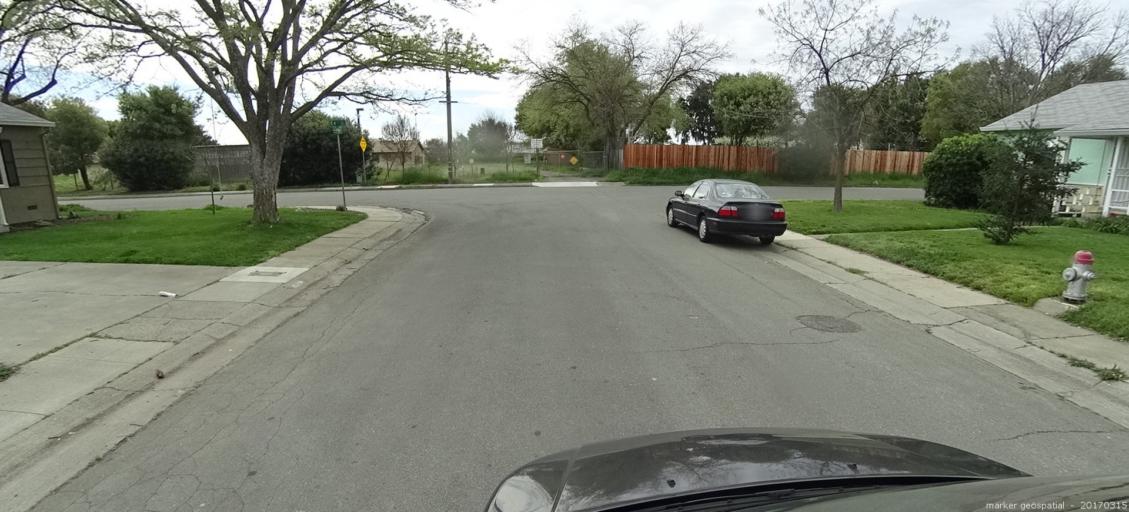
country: US
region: California
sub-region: Sacramento County
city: Parkway
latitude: 38.5221
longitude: -121.4956
